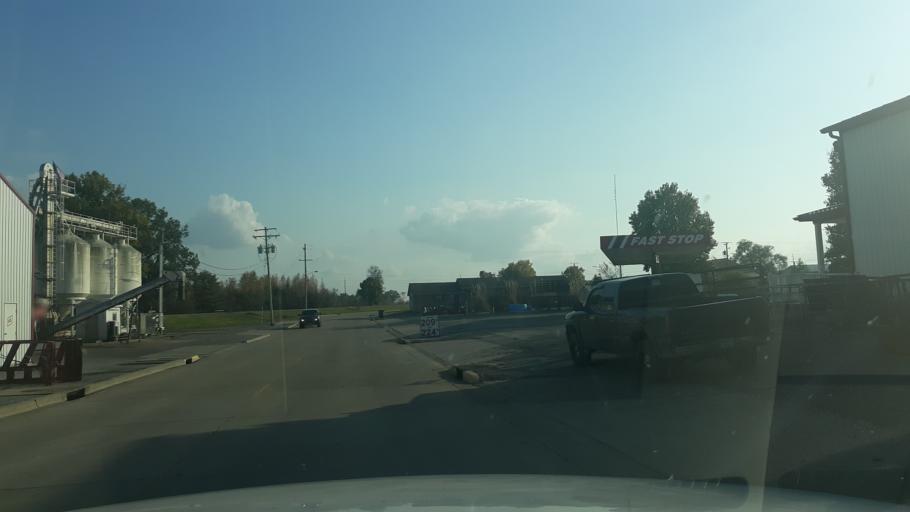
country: US
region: Illinois
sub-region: Saline County
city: Harrisburg
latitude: 37.7238
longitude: -88.5403
